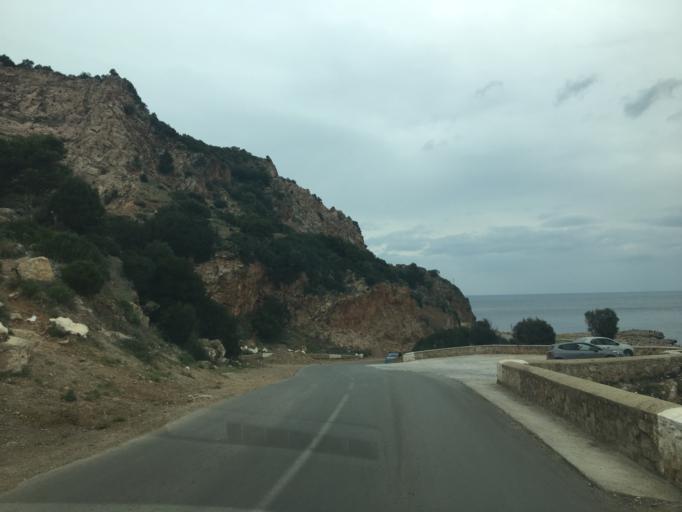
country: DZ
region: Tipaza
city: Tipasa
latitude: 36.6215
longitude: 2.4077
